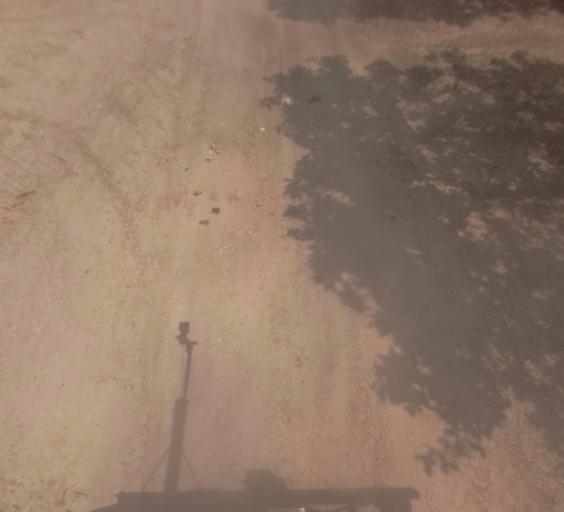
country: US
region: California
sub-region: Madera County
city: Fairmead
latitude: 37.1014
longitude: -120.1886
